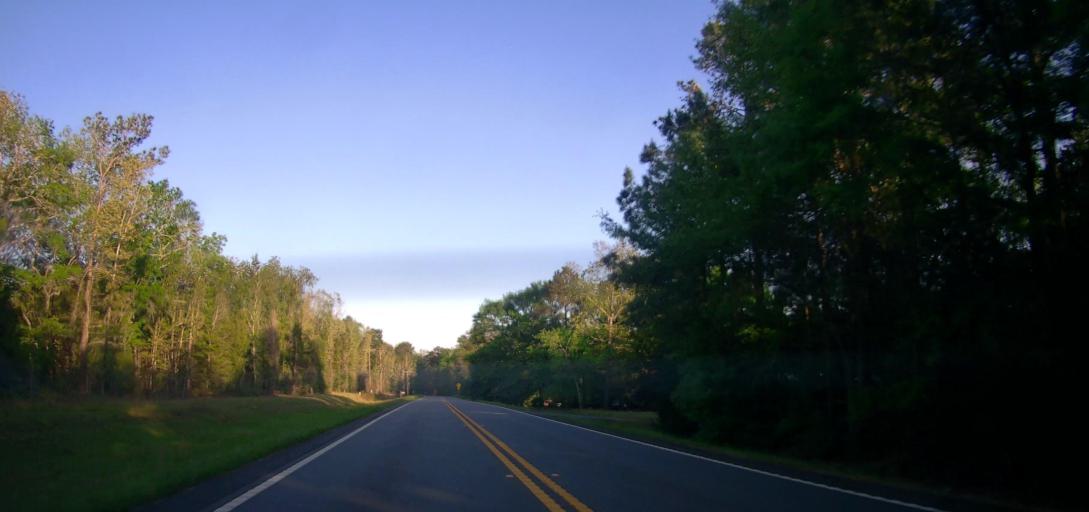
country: US
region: Georgia
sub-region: Schley County
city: Ellaville
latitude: 32.3184
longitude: -84.2587
